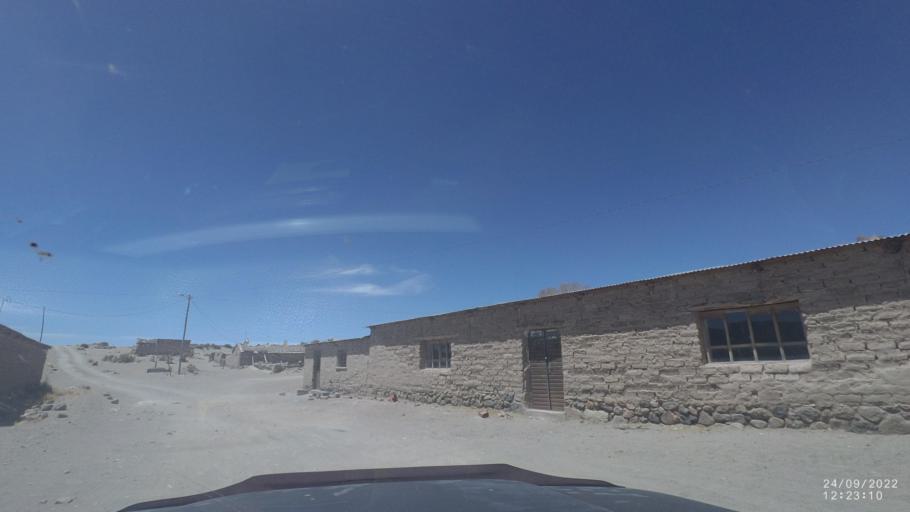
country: BO
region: Potosi
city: Colchani
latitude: -19.7614
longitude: -67.6642
